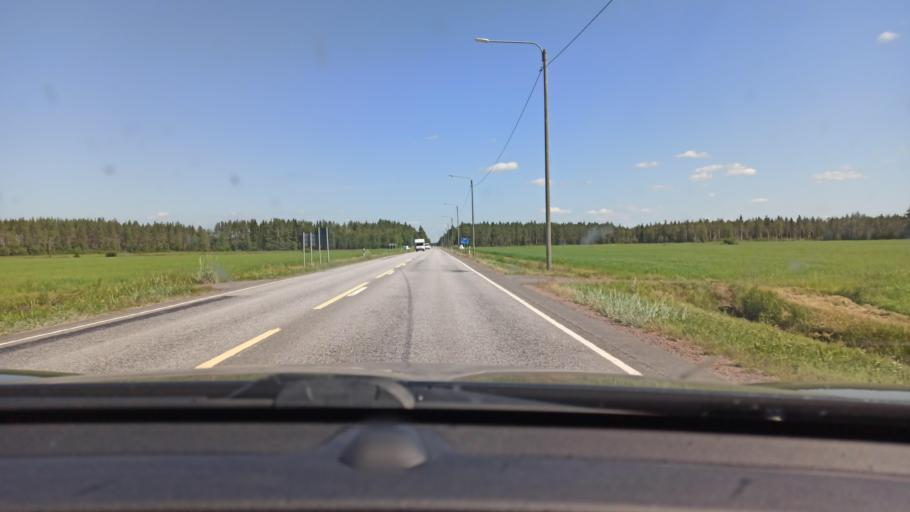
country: FI
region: Northern Ostrobothnia
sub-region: Raahe
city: Ruukki
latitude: 64.7214
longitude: 24.9897
